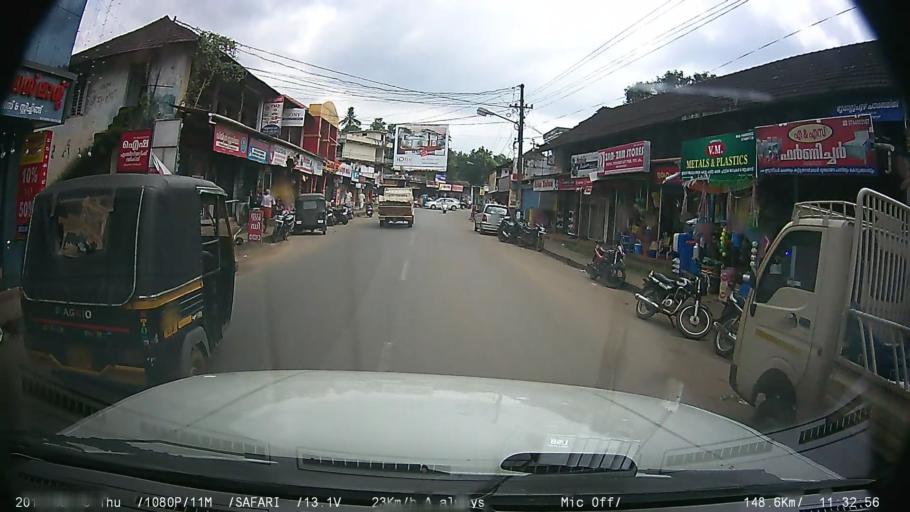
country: IN
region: Kerala
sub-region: Ernakulam
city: Muvattupula
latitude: 9.9918
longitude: 76.5842
